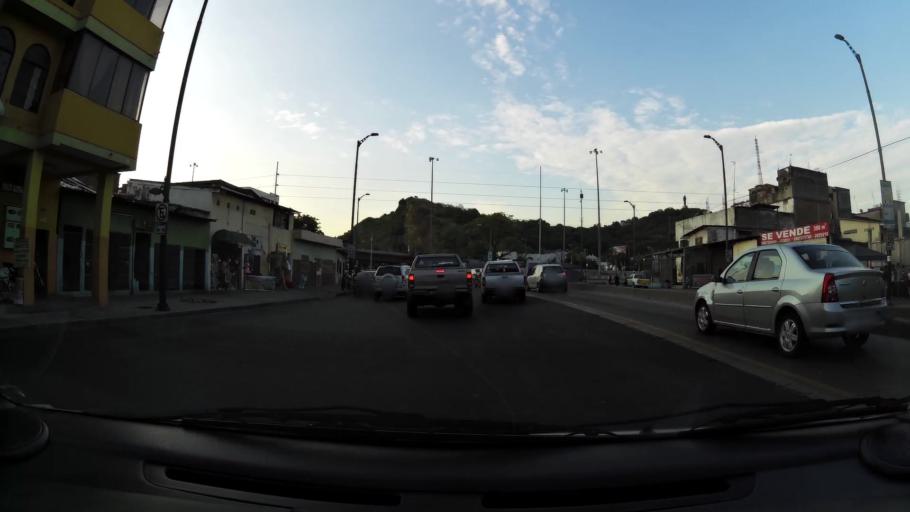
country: EC
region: Guayas
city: Guayaquil
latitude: -2.1850
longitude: -79.8878
